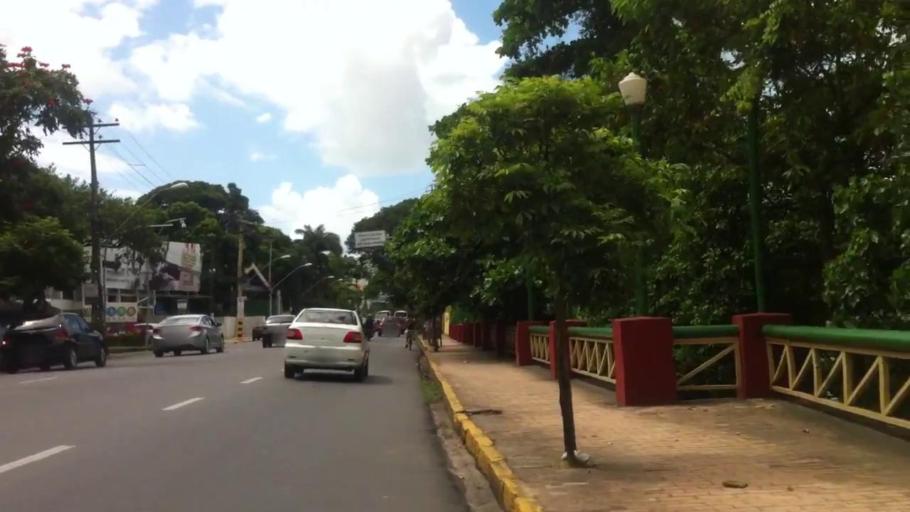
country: BR
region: Pernambuco
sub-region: Recife
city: Recife
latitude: -8.0391
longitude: -34.9047
